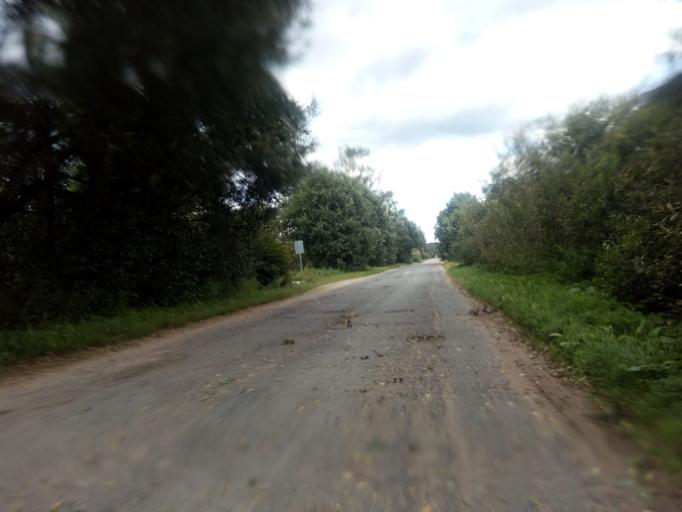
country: BY
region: Vitebsk
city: Dzisna
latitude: 55.7096
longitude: 28.3022
